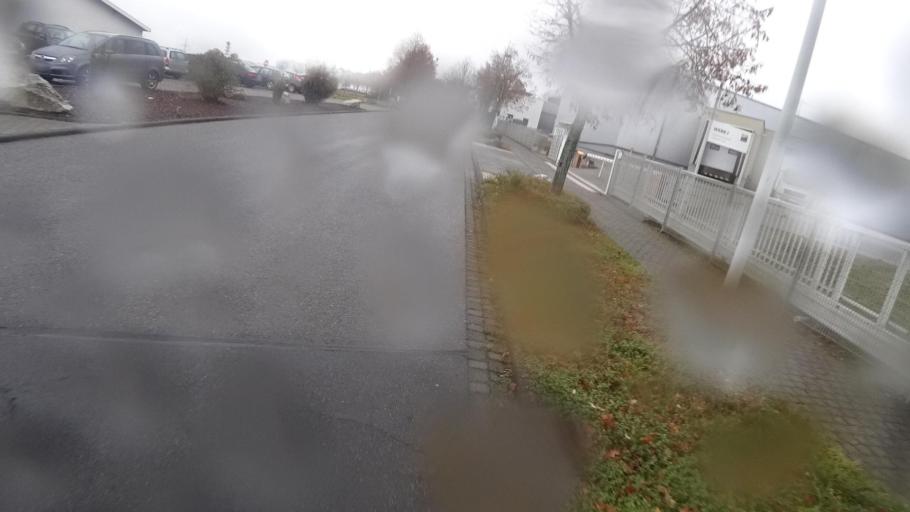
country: DE
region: Rheinland-Pfalz
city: Wiebelsheim
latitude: 50.0793
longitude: 7.6243
